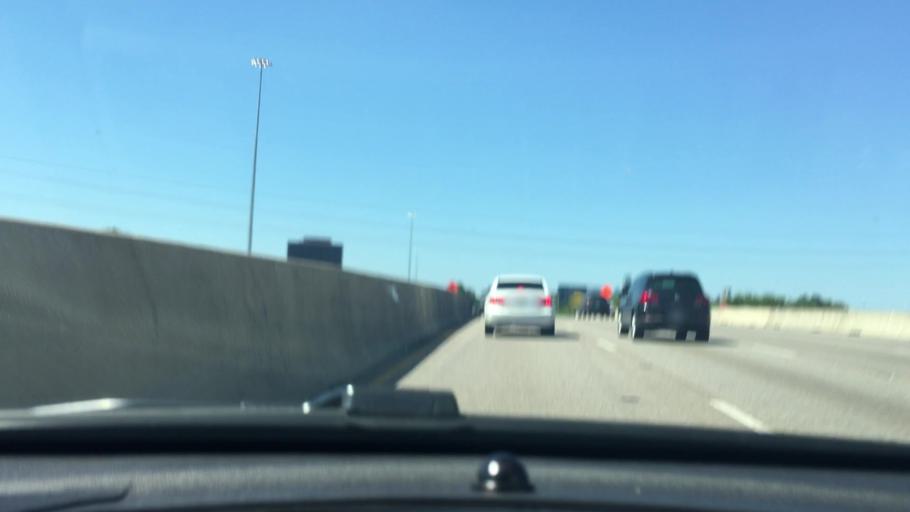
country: US
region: Texas
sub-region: Dallas County
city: Dallas
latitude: 32.7338
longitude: -96.8241
